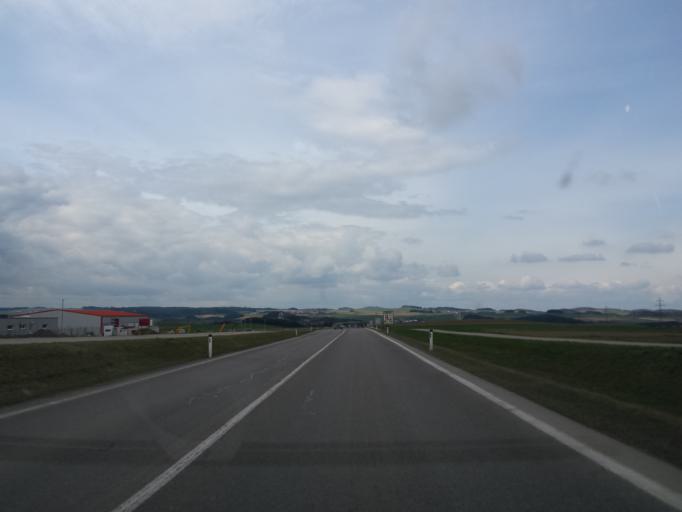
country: AT
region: Lower Austria
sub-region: Politischer Bezirk Krems
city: Jaidhof
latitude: 48.5256
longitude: 15.4658
